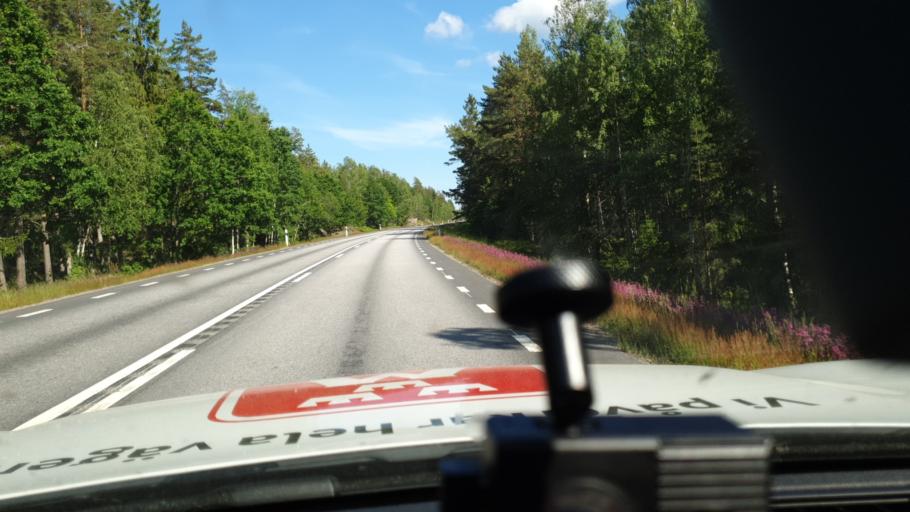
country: SE
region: Kalmar
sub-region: Vasterviks Kommun
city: Ankarsrum
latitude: 57.7140
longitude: 16.1091
